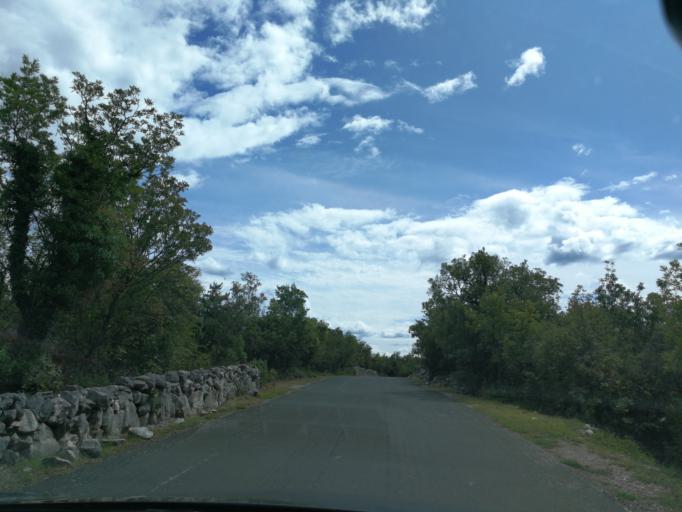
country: HR
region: Primorsko-Goranska
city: Omisalj
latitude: 45.1967
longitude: 14.5769
